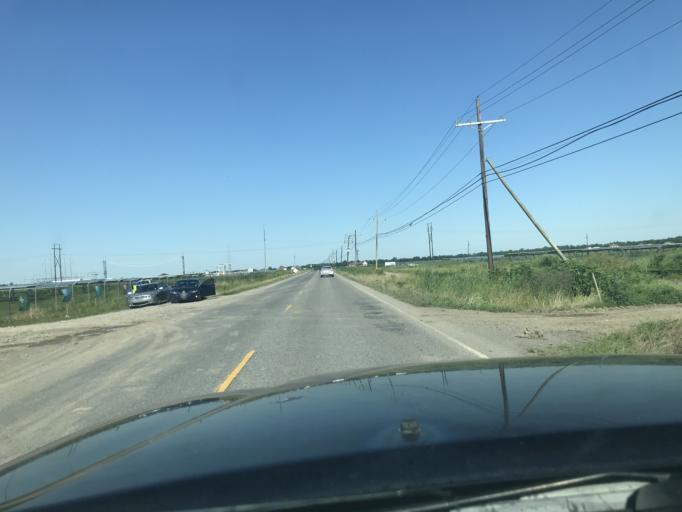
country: US
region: Louisiana
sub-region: West Baton Rouge Parish
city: Brusly
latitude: 30.4688
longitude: -91.3166
